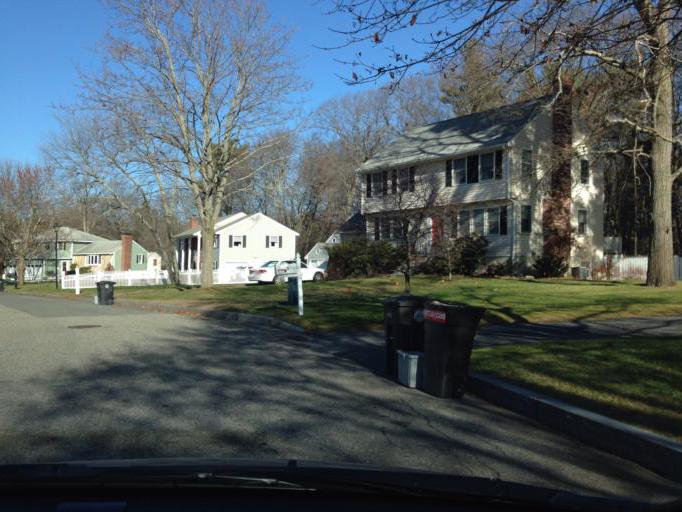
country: US
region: Massachusetts
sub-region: Middlesex County
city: Bedford
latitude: 42.4818
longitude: -71.2819
